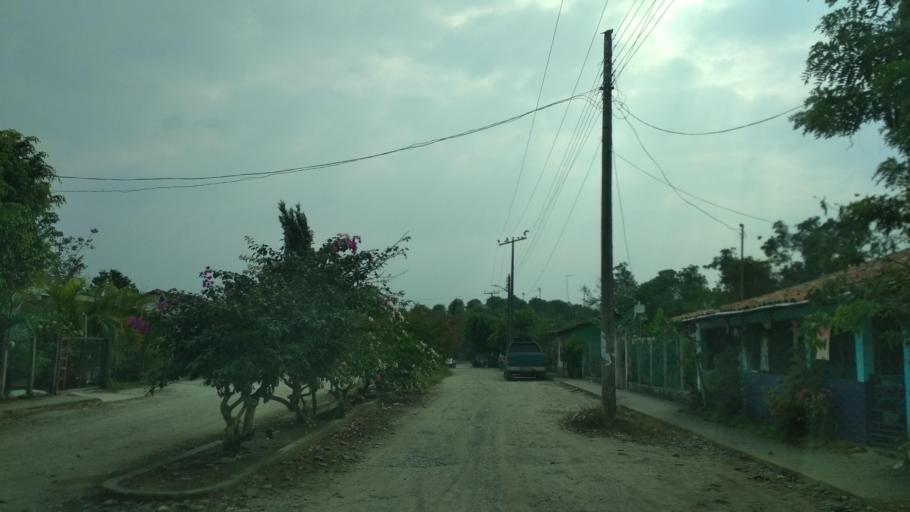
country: MM
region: Kayah
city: Loikaw
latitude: 20.2370
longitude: 97.2784
